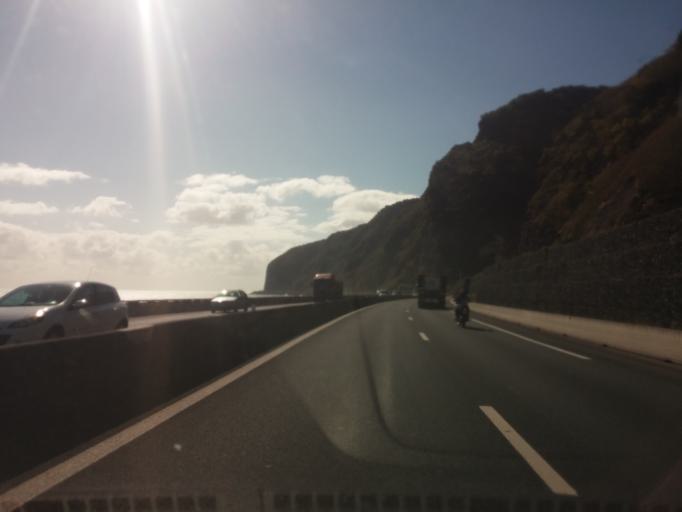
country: RE
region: Reunion
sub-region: Reunion
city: La Possession
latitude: -20.8921
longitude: 55.3809
